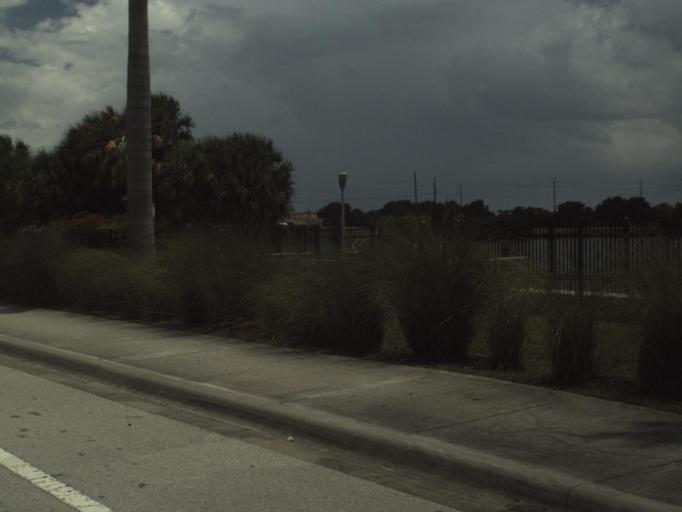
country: US
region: Florida
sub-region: Palm Beach County
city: West Palm Beach
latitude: 26.7057
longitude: -80.0689
